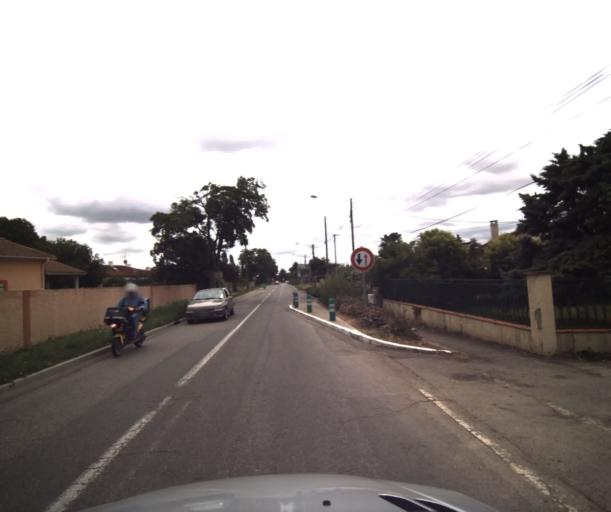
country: FR
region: Midi-Pyrenees
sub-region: Departement de la Haute-Garonne
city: Pinsaguel
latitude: 43.4986
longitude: 1.3927
